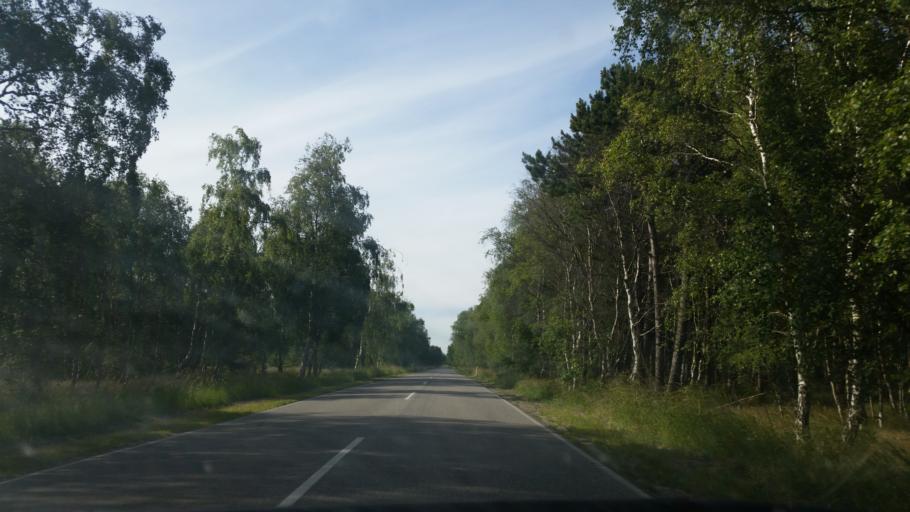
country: DK
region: Central Jutland
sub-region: Samso Kommune
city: Tranebjerg
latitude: 55.9323
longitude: 10.5837
